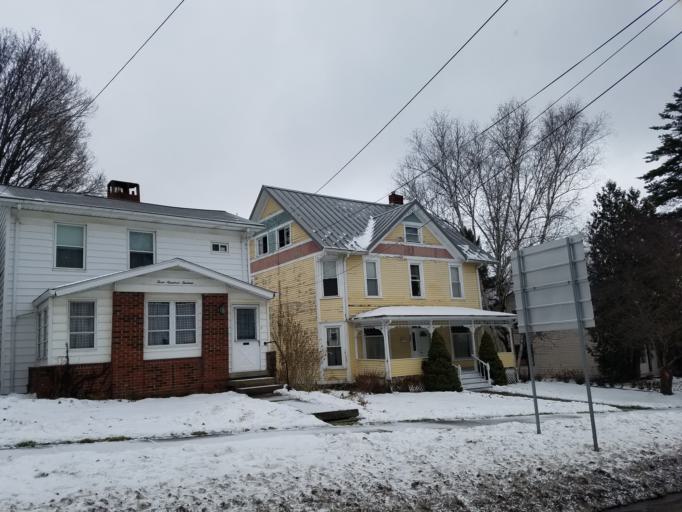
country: US
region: Pennsylvania
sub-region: Mercer County
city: Mercer
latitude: 41.2270
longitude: -80.2345
